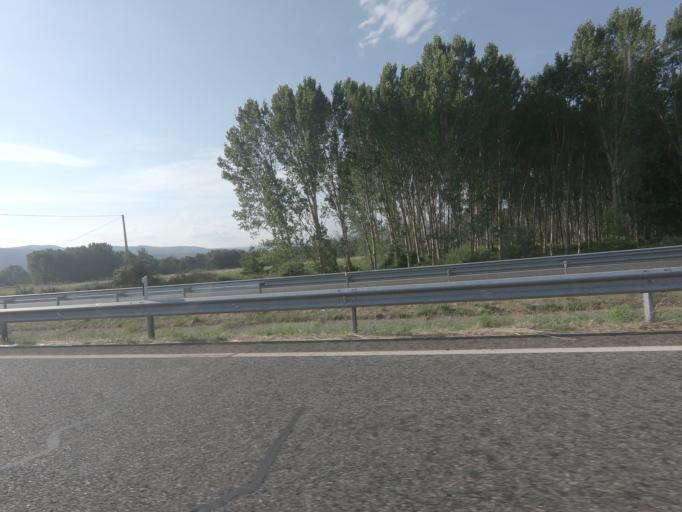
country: ES
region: Galicia
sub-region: Provincia de Ourense
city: Oimbra
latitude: 41.9224
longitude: -7.4745
